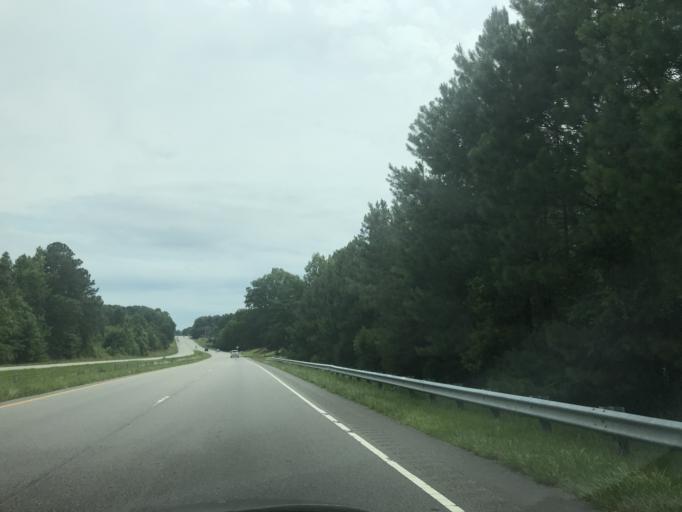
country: US
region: North Carolina
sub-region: Vance County
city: South Henderson
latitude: 36.2311
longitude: -78.4406
